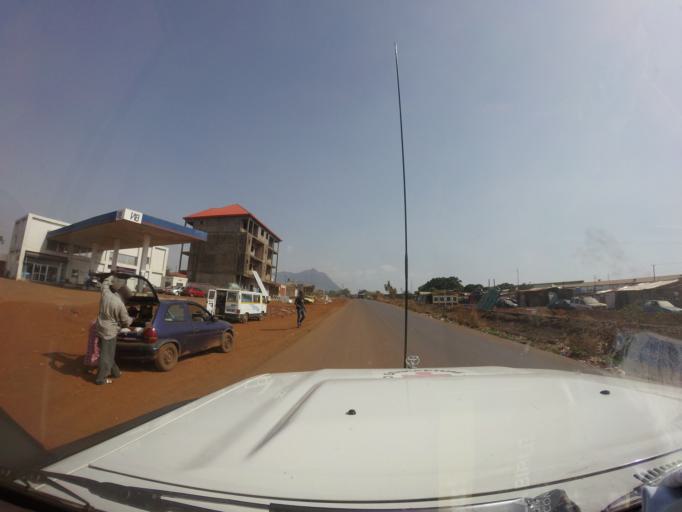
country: GN
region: Kindia
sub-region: Prefecture de Dubreka
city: Dubreka
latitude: 9.7138
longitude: -13.4860
